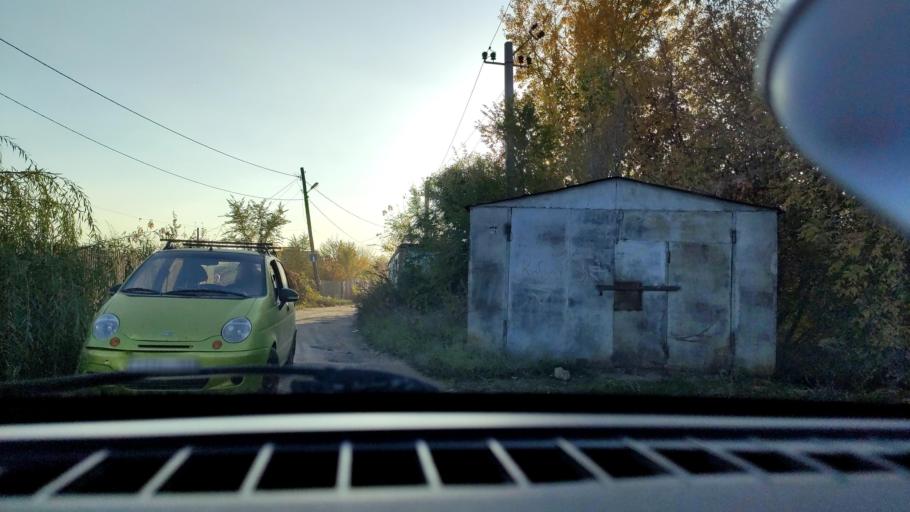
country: RU
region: Samara
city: Samara
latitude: 53.1820
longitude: 50.2241
